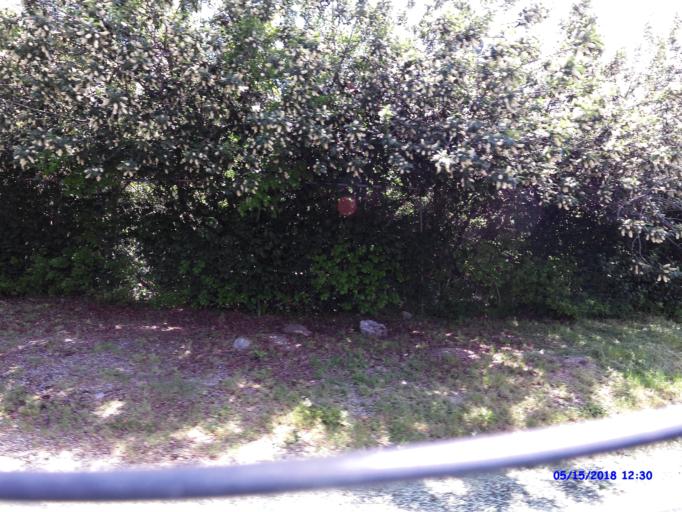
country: US
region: Utah
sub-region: Weber County
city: Uintah
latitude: 41.1767
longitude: -111.9299
